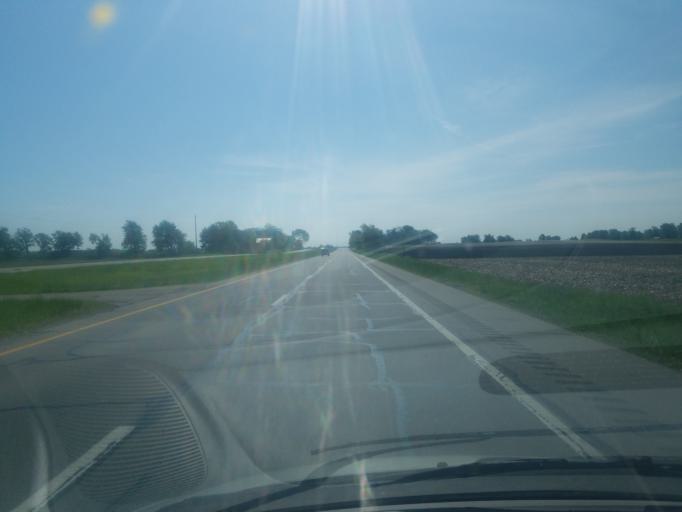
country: US
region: Ohio
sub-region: Huron County
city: Monroeville
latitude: 41.2570
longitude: -82.7516
